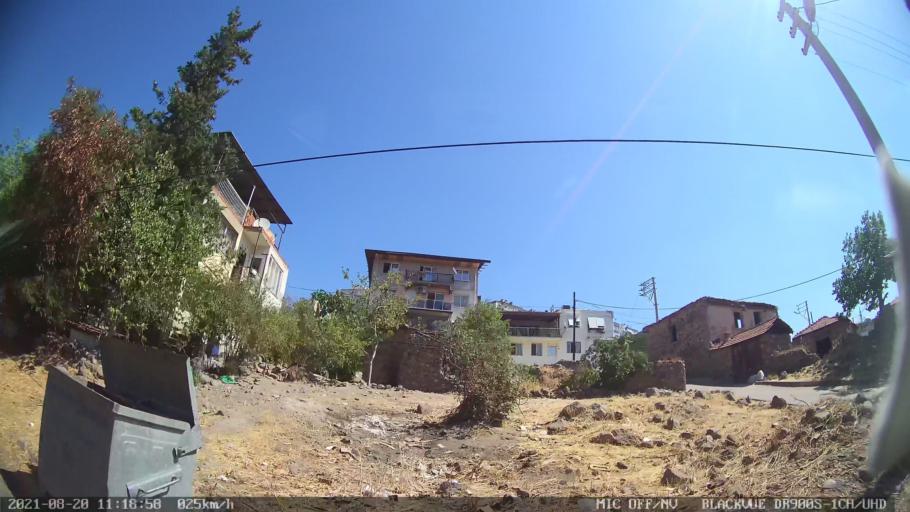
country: TR
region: Izmir
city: Karsiyaka
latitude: 38.5018
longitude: 27.0693
